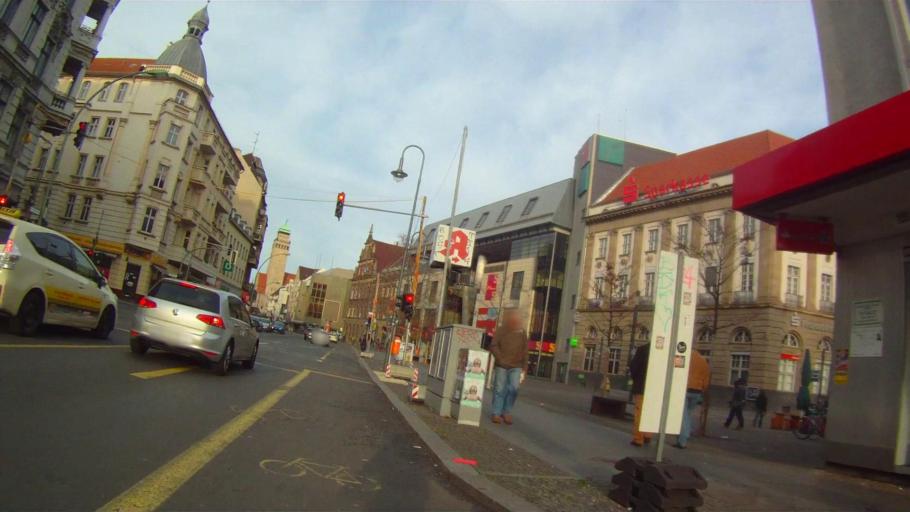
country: DE
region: Berlin
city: Berlin Treptow
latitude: 52.4788
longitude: 13.4378
